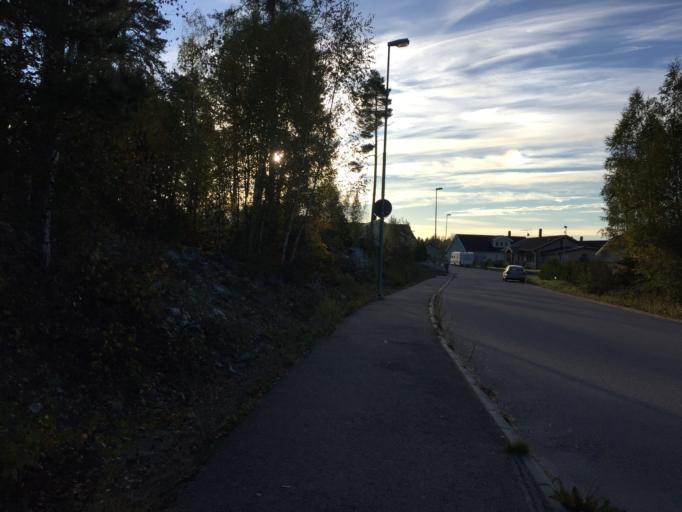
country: SE
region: Vaestmanland
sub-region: Hallstahammars Kommun
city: Hallstahammar
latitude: 59.6304
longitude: 16.2346
